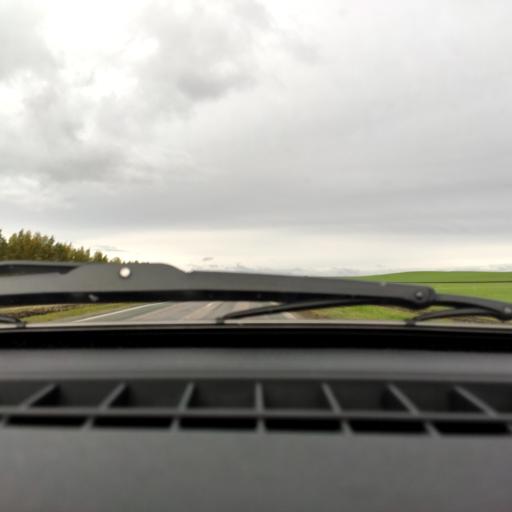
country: RU
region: Bashkortostan
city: Rayevskiy
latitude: 54.1465
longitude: 54.9471
